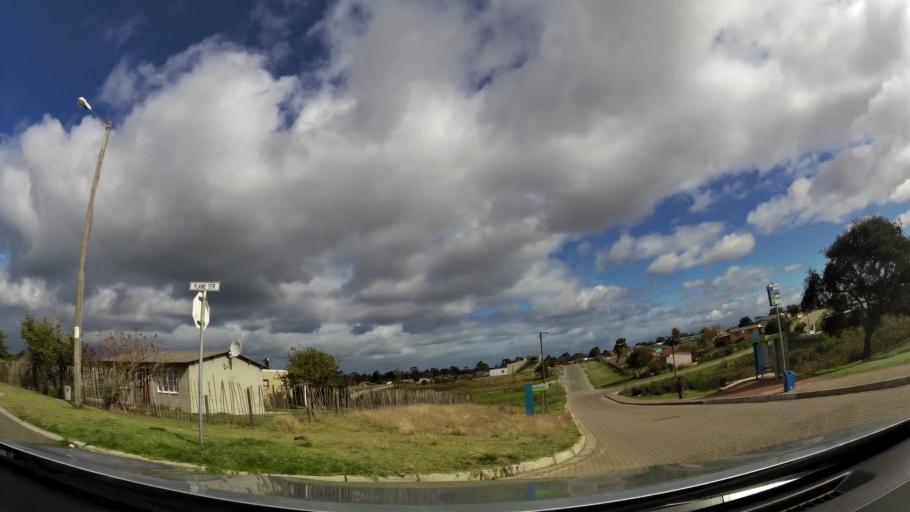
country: ZA
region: Western Cape
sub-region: Eden District Municipality
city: George
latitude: -34.0236
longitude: 22.4692
